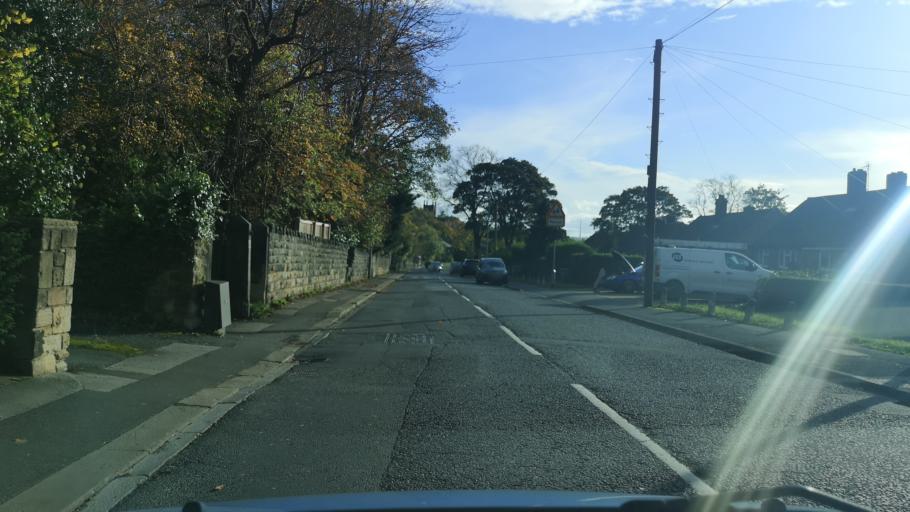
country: GB
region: England
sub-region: Kirklees
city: Batley
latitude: 53.6960
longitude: -1.6518
